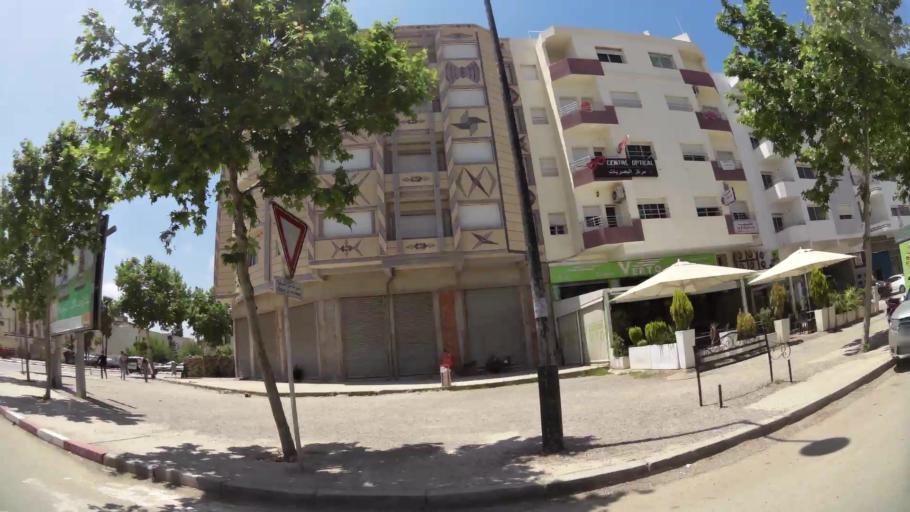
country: MA
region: Fes-Boulemane
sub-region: Fes
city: Fes
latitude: 34.0181
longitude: -5.0529
